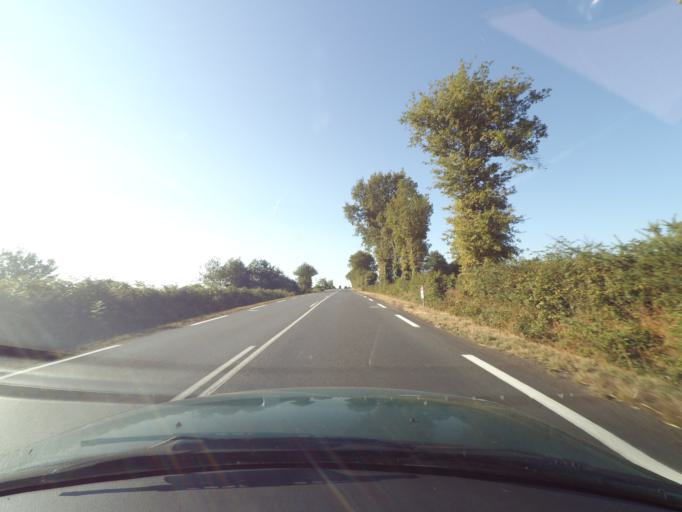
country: FR
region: Poitou-Charentes
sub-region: Departement des Deux-Sevres
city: Viennay
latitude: 46.7348
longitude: -0.3008
